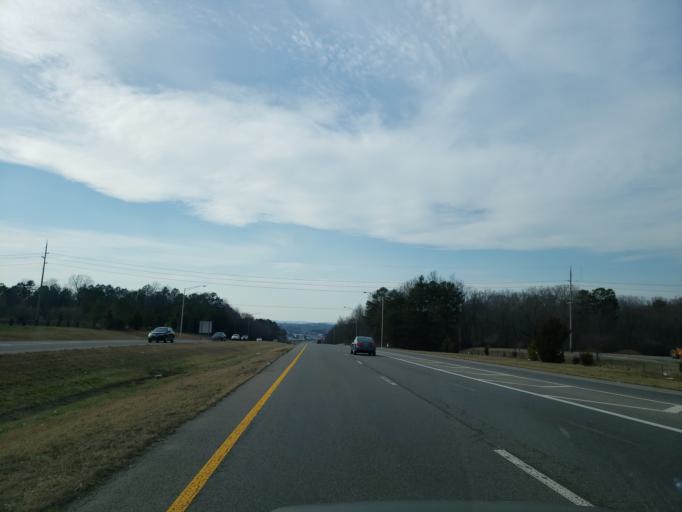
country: US
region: Tennessee
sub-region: Bradley County
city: East Cleveland
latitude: 35.1697
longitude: -84.8497
